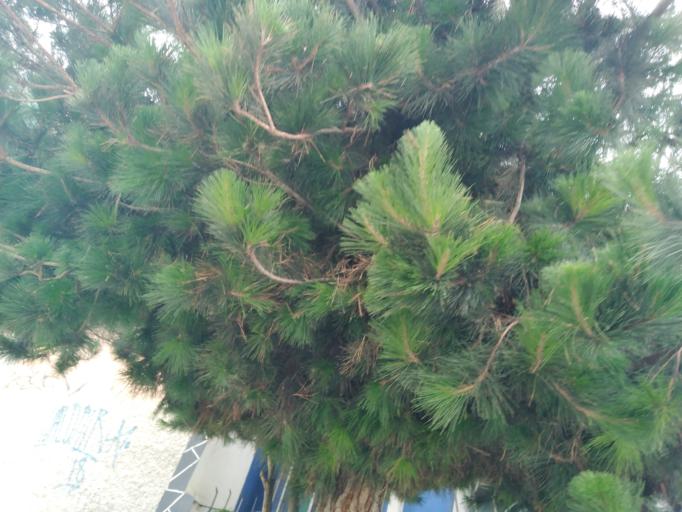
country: BO
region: La Paz
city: La Paz
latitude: -16.5118
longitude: -68.1375
